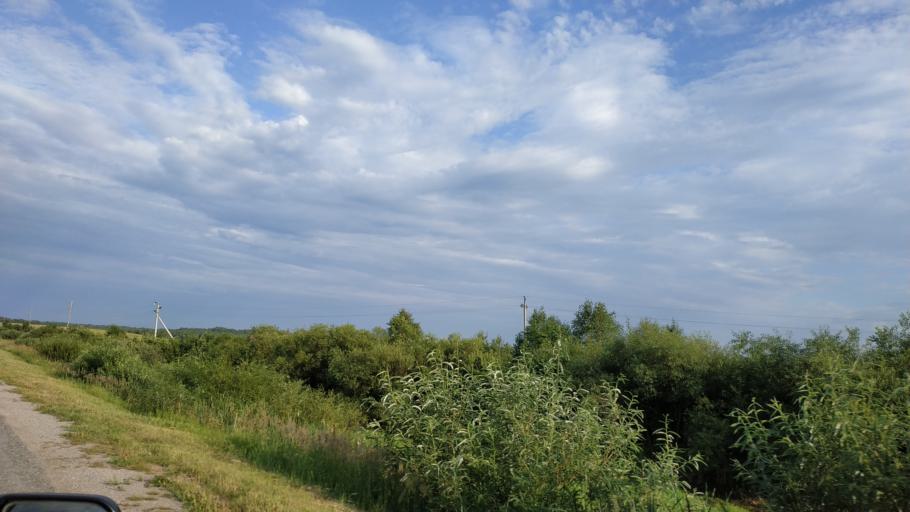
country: RU
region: Sverdlovsk
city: Yelanskiy
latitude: 57.0808
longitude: 62.4897
